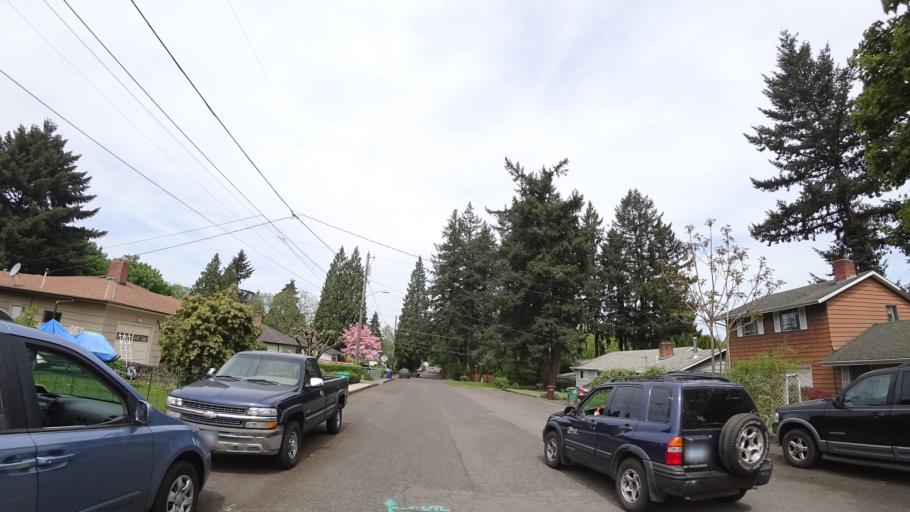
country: US
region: Oregon
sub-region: Clackamas County
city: Milwaukie
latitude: 45.4523
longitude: -122.6223
